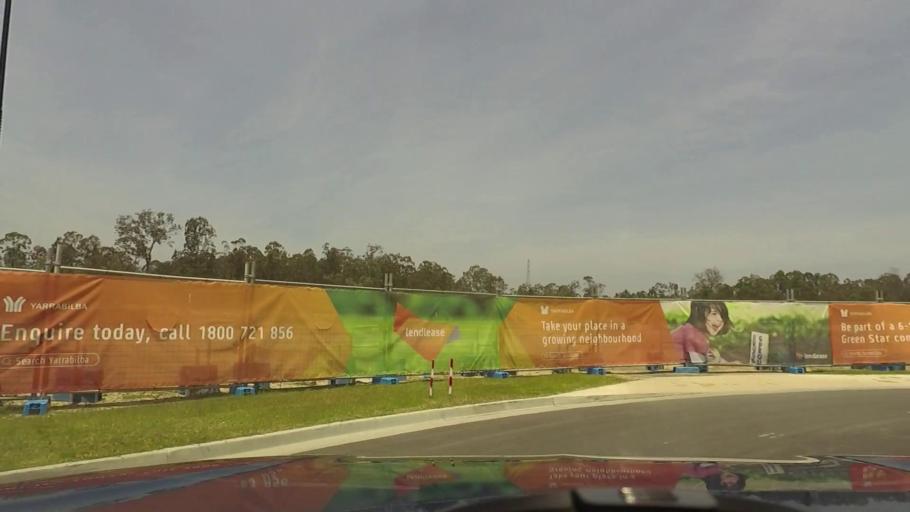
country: AU
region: Queensland
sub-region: Logan
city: Chambers Flat
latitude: -27.8096
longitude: 153.1240
